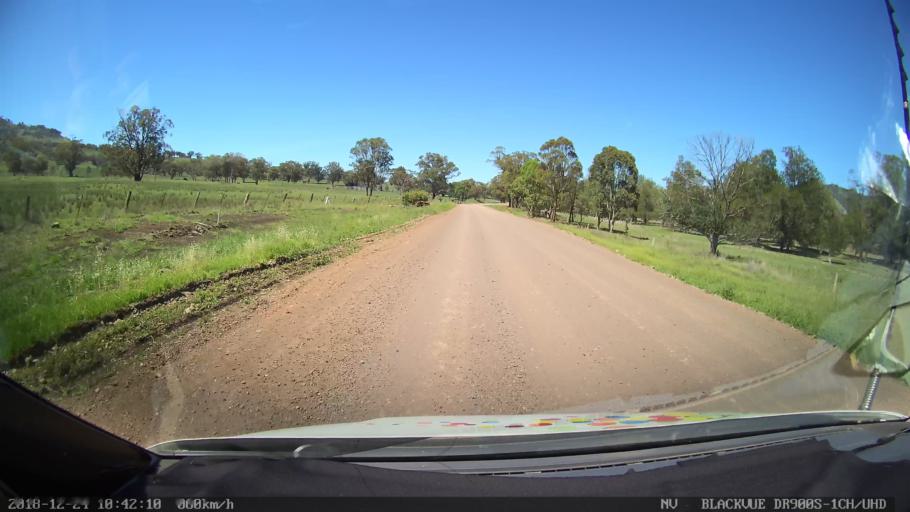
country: AU
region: New South Wales
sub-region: Upper Hunter Shire
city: Merriwa
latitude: -31.8745
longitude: 150.4547
